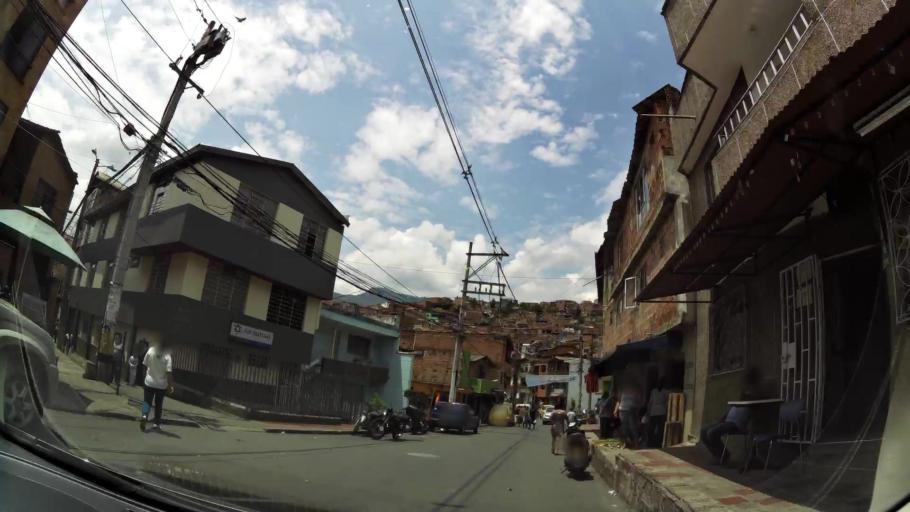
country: CO
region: Antioquia
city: Medellin
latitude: 6.2596
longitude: -75.6175
